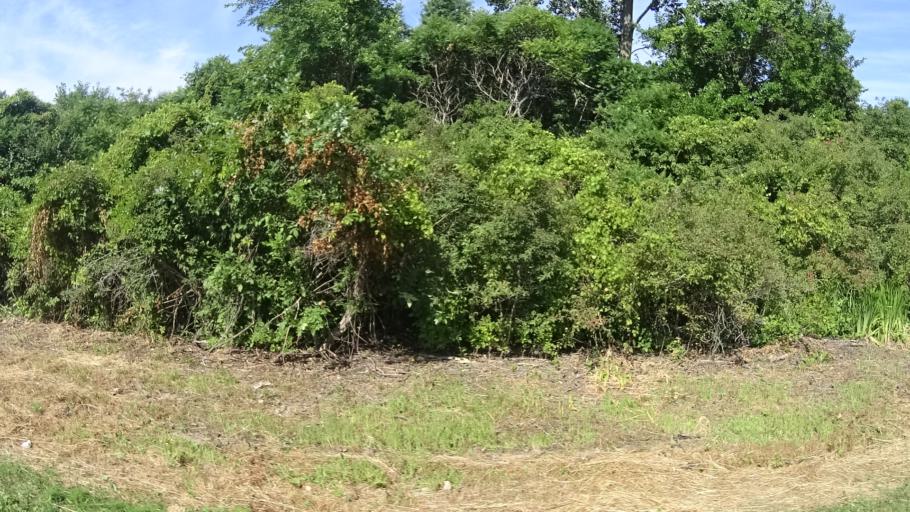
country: US
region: Ohio
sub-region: Erie County
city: Huron
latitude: 41.4232
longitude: -82.6260
